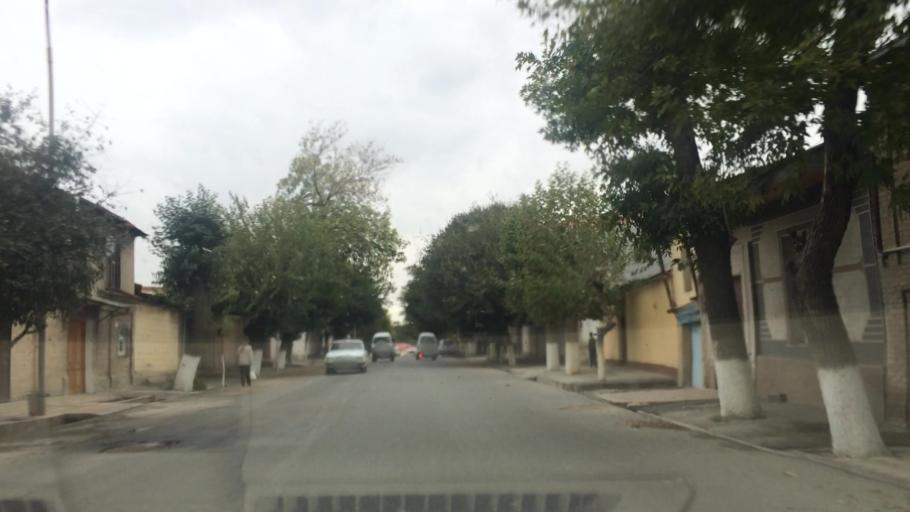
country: UZ
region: Samarqand
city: Samarqand
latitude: 39.6596
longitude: 66.9732
